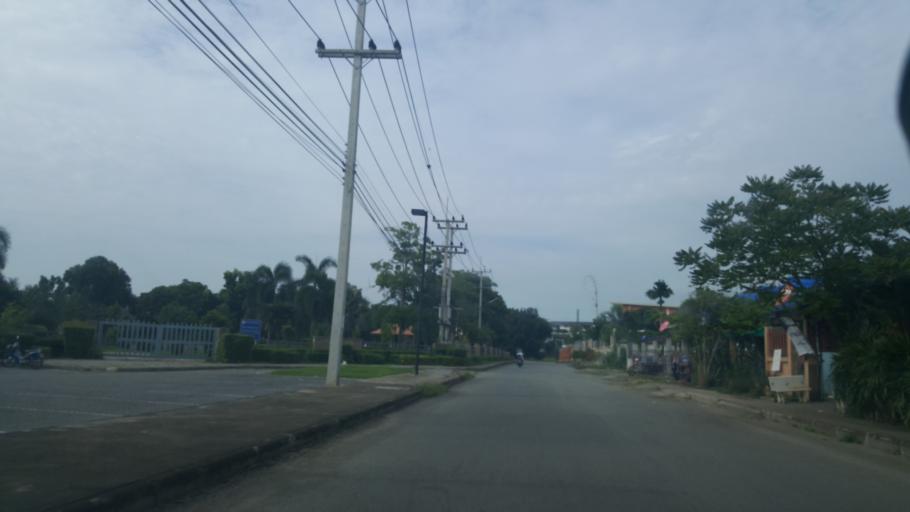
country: TH
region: Chon Buri
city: Sattahip
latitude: 12.6698
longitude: 100.9014
